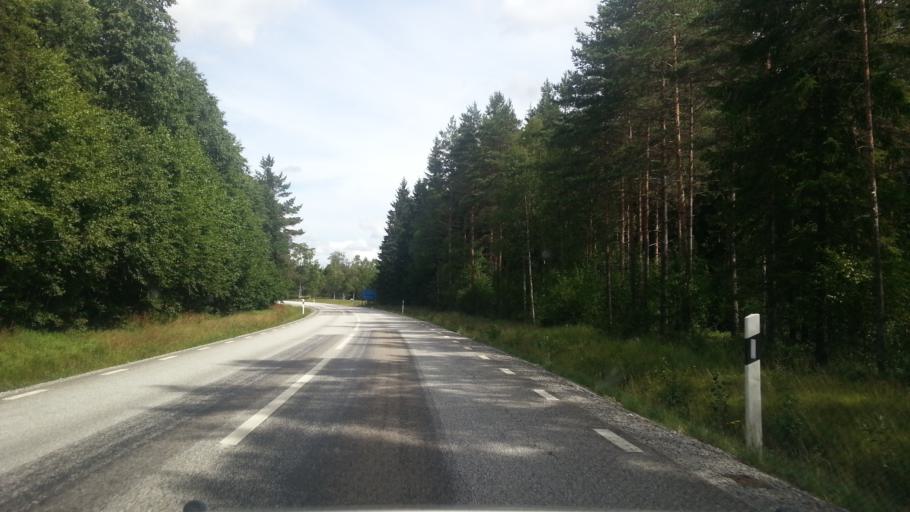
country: SE
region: Vaestmanland
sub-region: Skinnskattebergs Kommun
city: Skinnskatteberg
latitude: 59.7744
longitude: 15.5399
